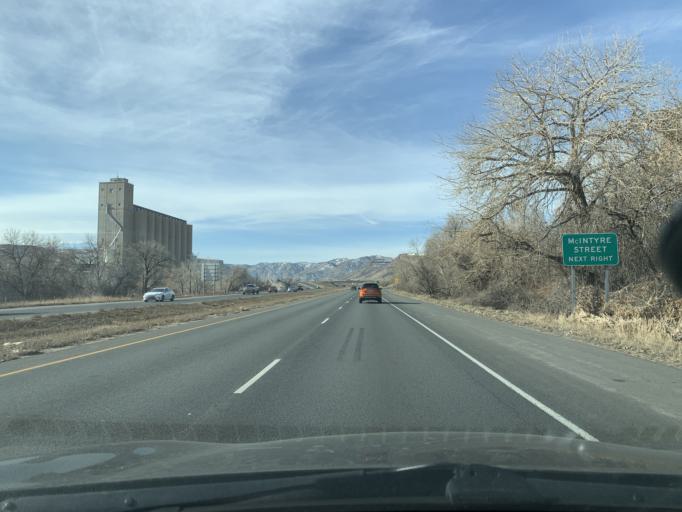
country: US
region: Colorado
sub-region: Jefferson County
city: Applewood
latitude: 39.7739
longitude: -105.1676
